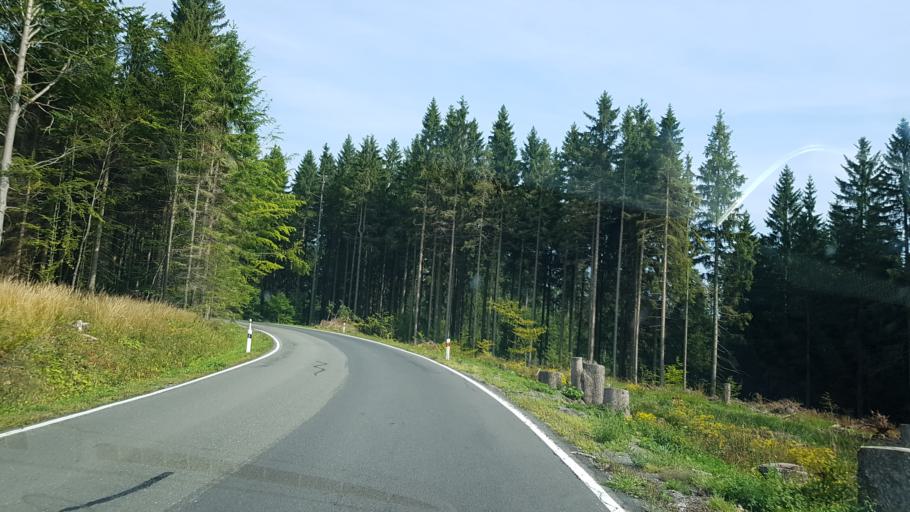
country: CZ
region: Olomoucky
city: Pisecna
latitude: 50.2194
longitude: 17.2741
